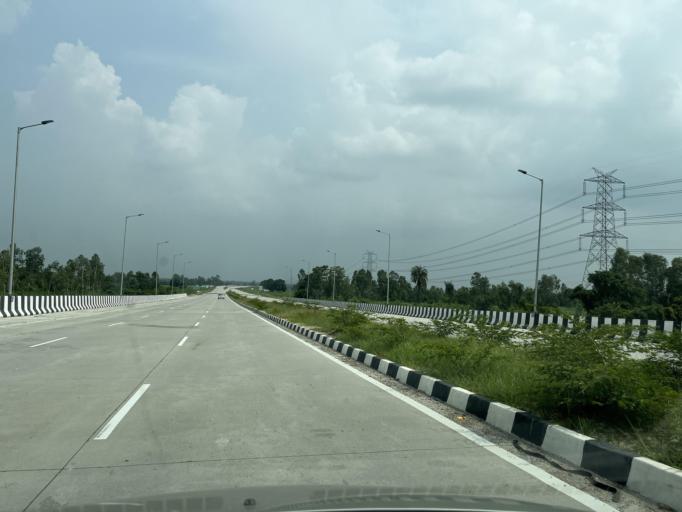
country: IN
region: Uttarakhand
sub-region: Udham Singh Nagar
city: Jaspur
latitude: 29.2936
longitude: 78.8451
